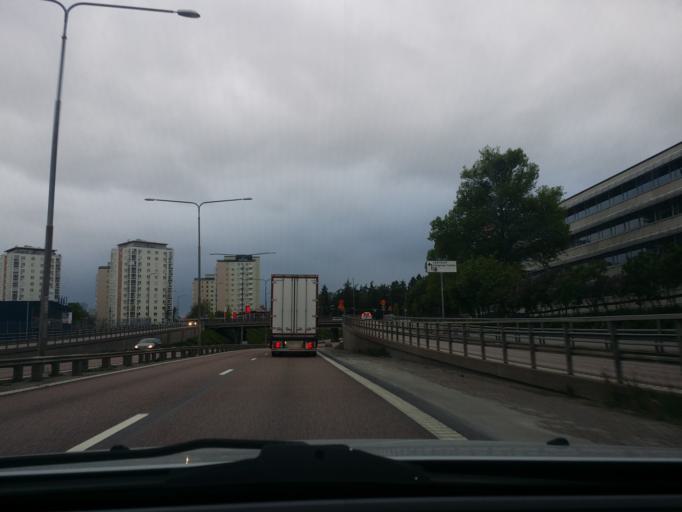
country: SE
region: Vaestmanland
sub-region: Vasteras
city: Vasteras
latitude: 59.6187
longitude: 16.5590
